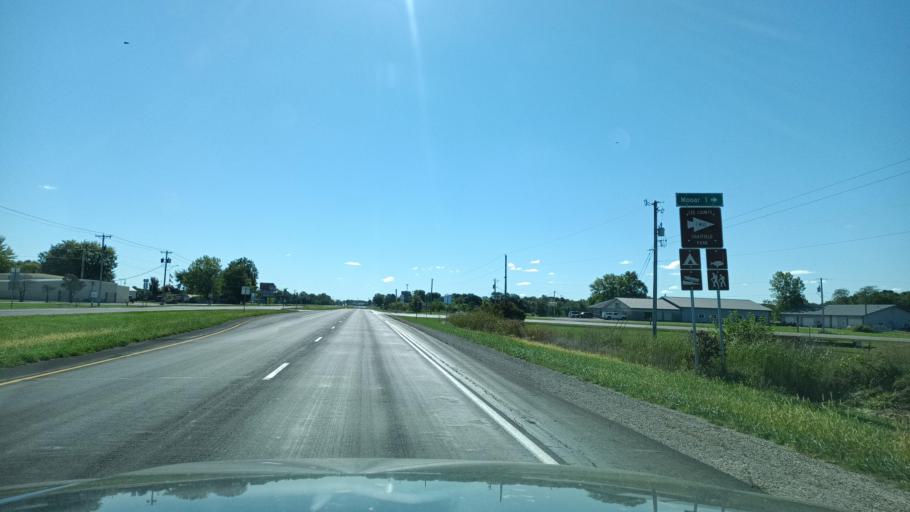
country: US
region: Iowa
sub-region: Lee County
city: Keokuk
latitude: 40.4449
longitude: -91.4397
